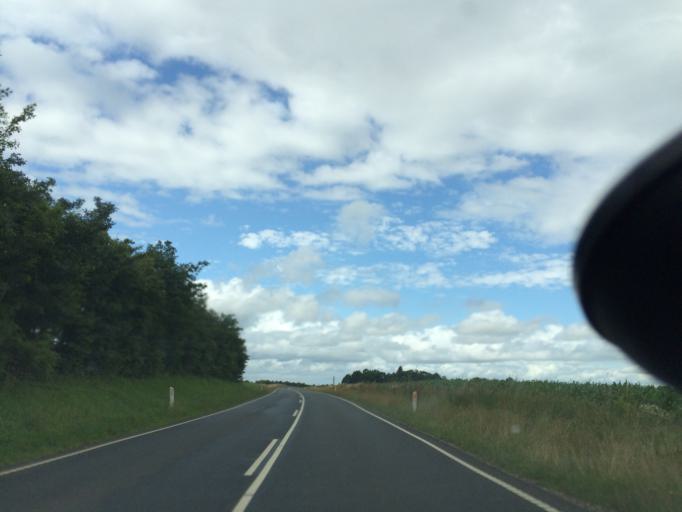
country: DK
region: Central Jutland
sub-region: Skanderborg Kommune
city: Ry
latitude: 56.1815
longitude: 9.7485
